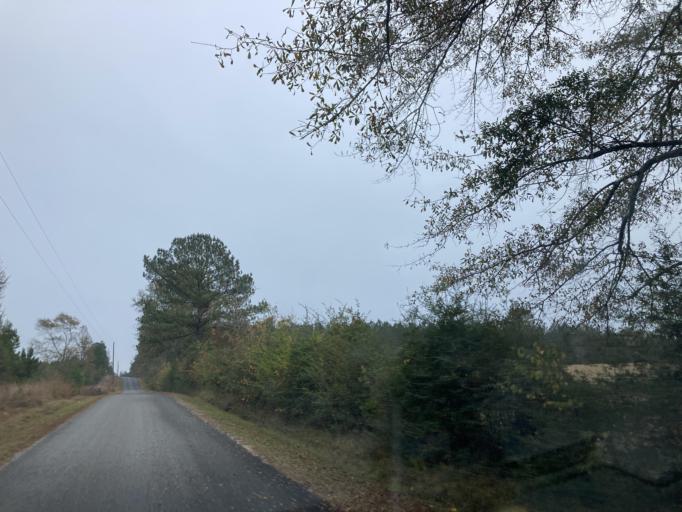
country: US
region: Mississippi
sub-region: Lamar County
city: Lumberton
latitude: 31.0249
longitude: -89.3594
